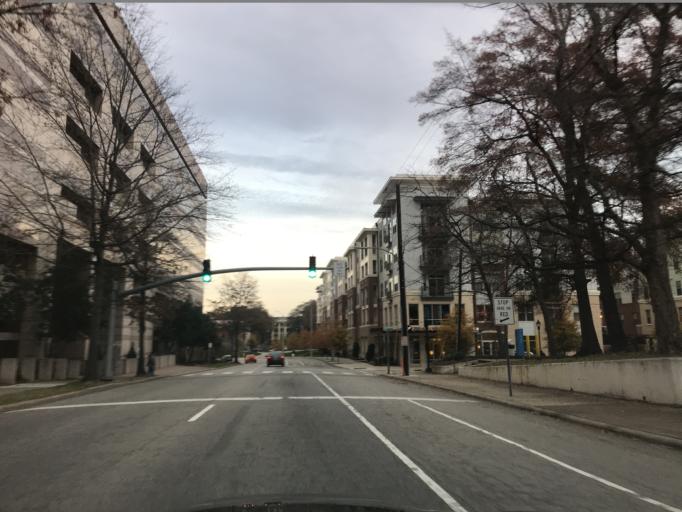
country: US
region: North Carolina
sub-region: Wake County
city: Raleigh
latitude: 35.7856
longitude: -78.6378
